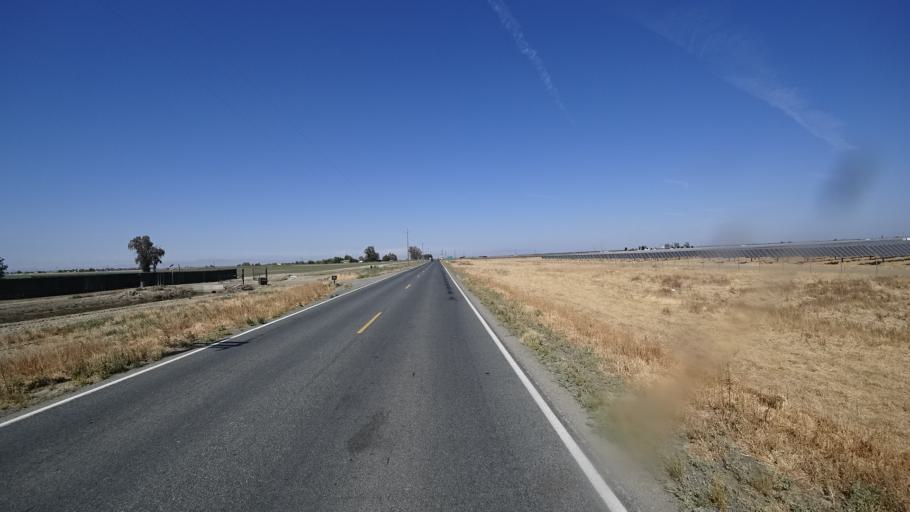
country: US
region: California
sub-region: Kings County
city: Stratford
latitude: 36.2115
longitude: -119.8108
